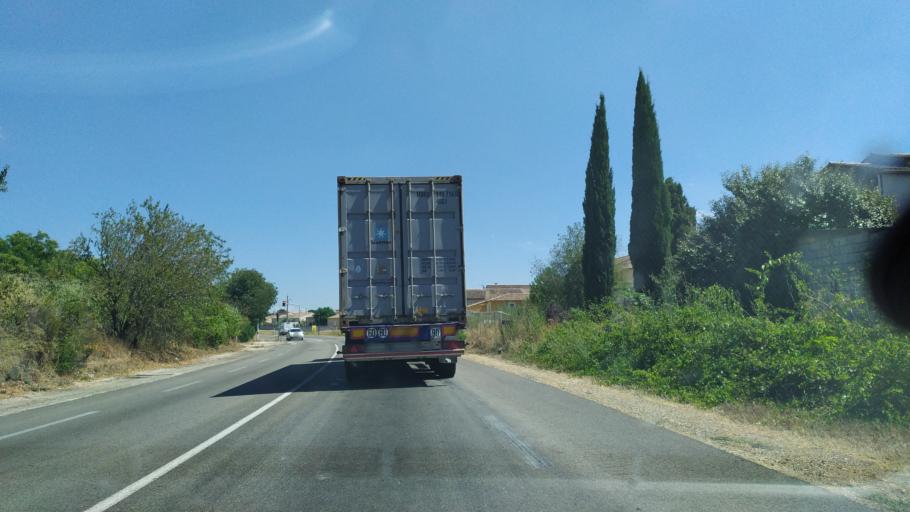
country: FR
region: Languedoc-Roussillon
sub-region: Departement du Gard
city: Caissargues
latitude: 43.7919
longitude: 4.3797
